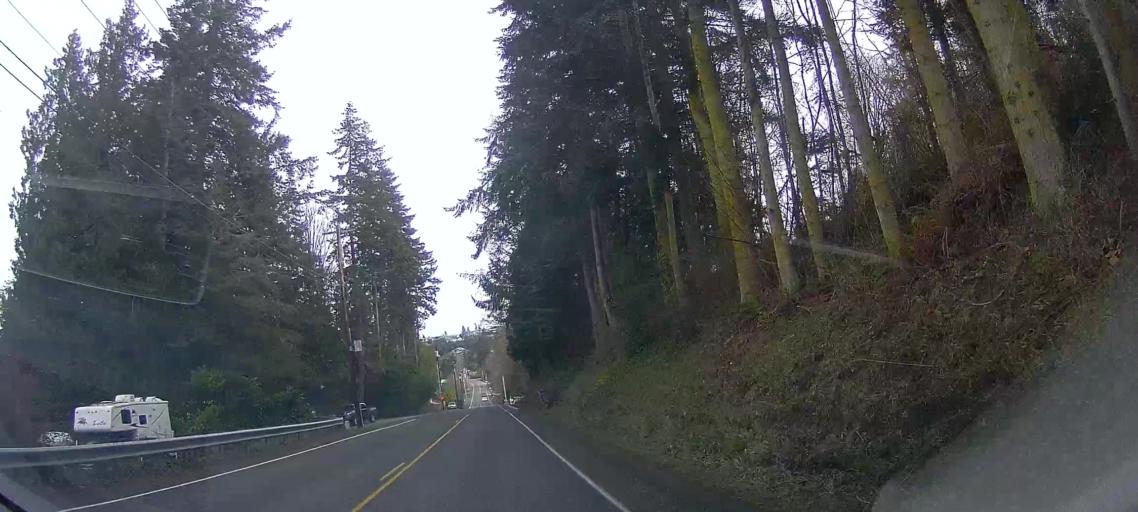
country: US
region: Washington
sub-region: Island County
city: Camano
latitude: 48.2504
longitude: -122.4889
